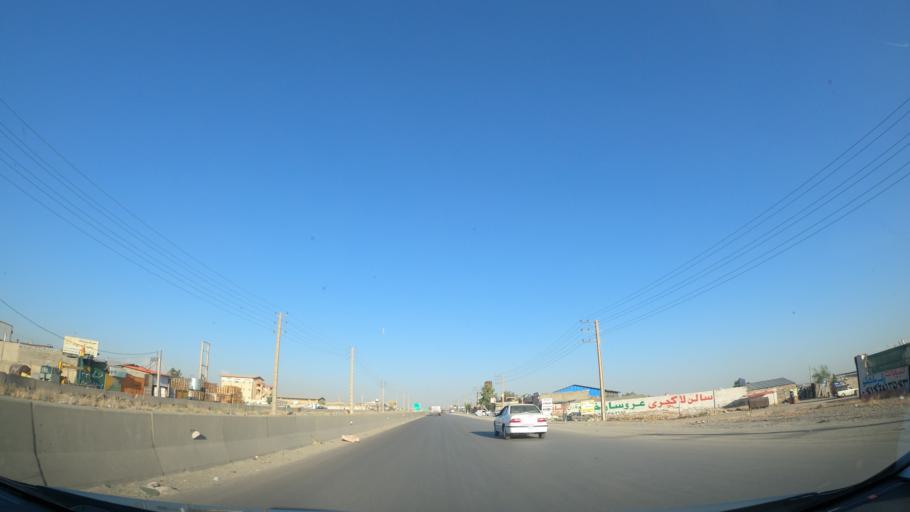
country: IR
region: Alborz
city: Hashtgerd
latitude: 35.9163
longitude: 50.7560
